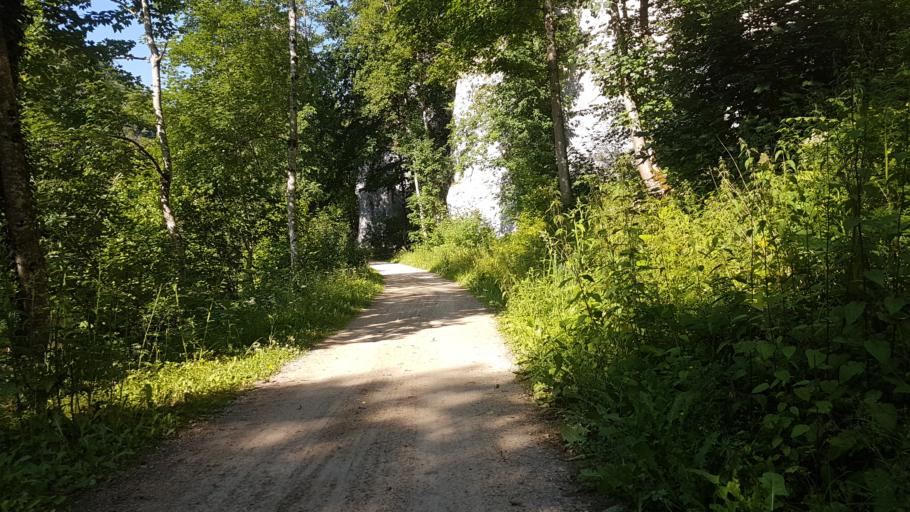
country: DE
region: Baden-Wuerttemberg
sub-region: Tuebingen Region
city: Stetten am Kalten Markt
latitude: 48.0797
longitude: 9.0861
